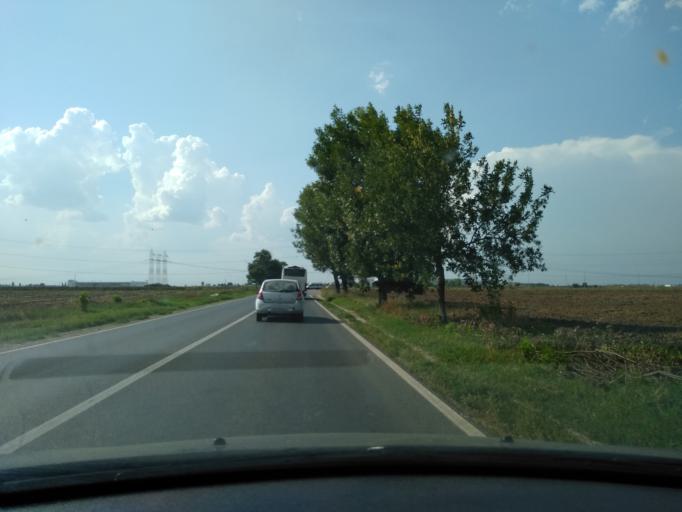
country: RO
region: Ilfov
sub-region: Comuna Glina
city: Glina
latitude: 44.3475
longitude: 26.2220
